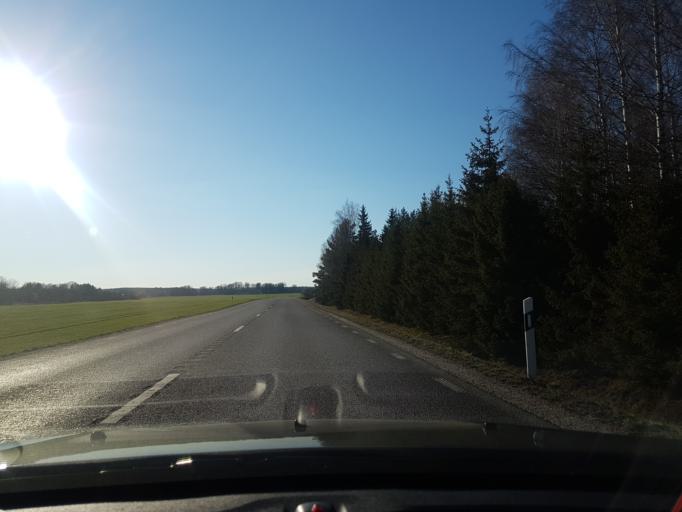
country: SE
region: Uppsala
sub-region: Enkopings Kommun
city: Orsundsbro
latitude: 59.8707
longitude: 17.3089
